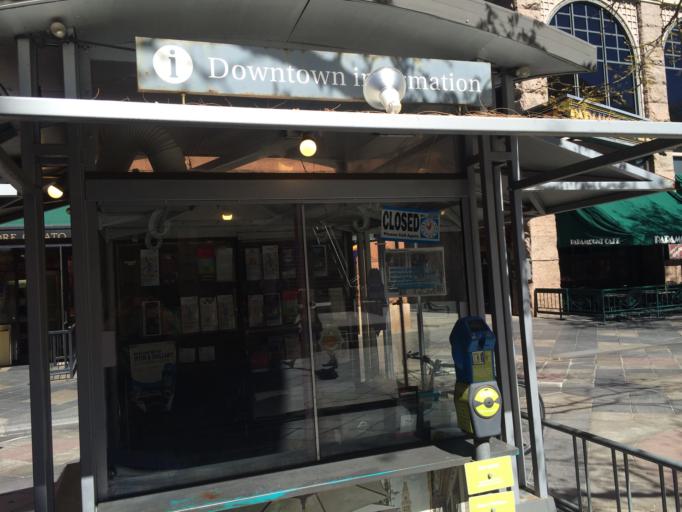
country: US
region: Colorado
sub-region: Denver County
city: Denver
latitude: 39.7443
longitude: -104.9908
